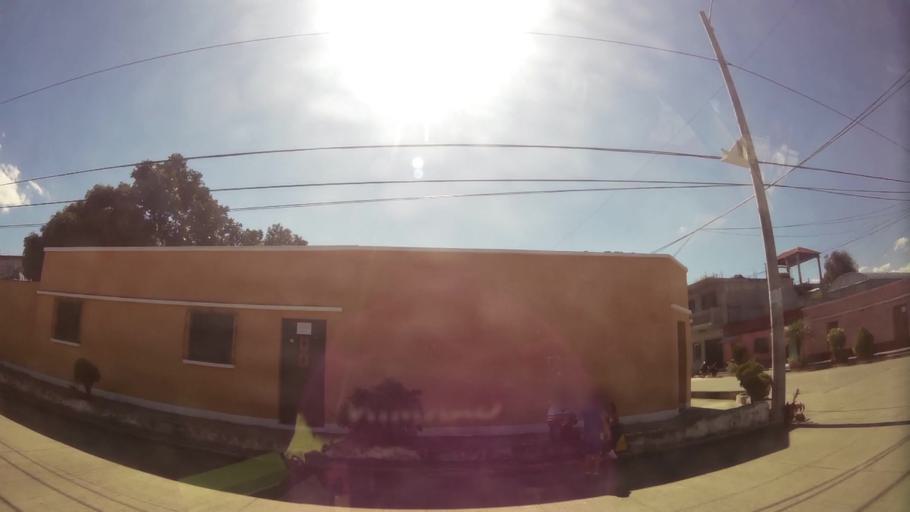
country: GT
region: Guatemala
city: Petapa
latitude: 14.5068
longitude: -90.5671
